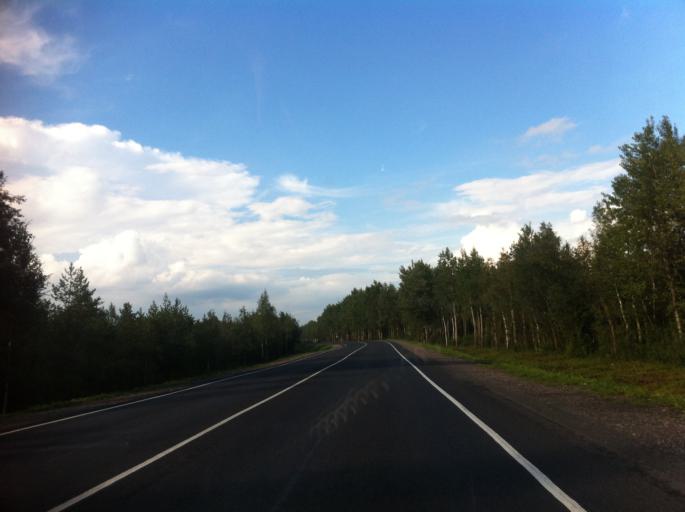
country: RU
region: Leningrad
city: Luga
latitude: 58.4400
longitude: 29.7511
